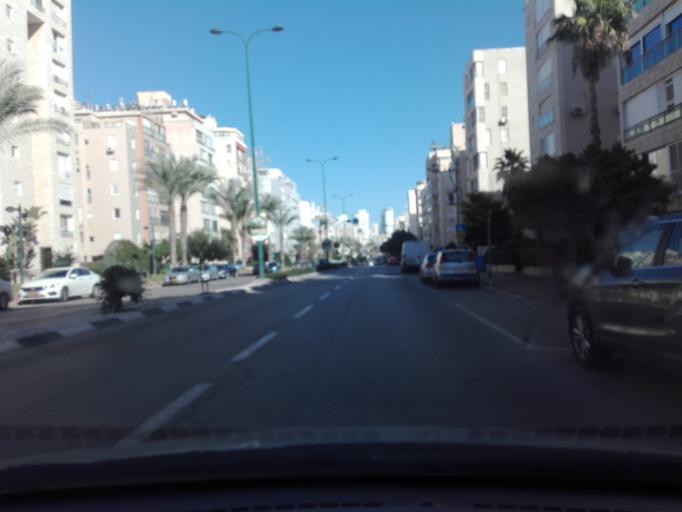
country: IL
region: Central District
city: Netanya
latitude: 32.3204
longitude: 34.8483
